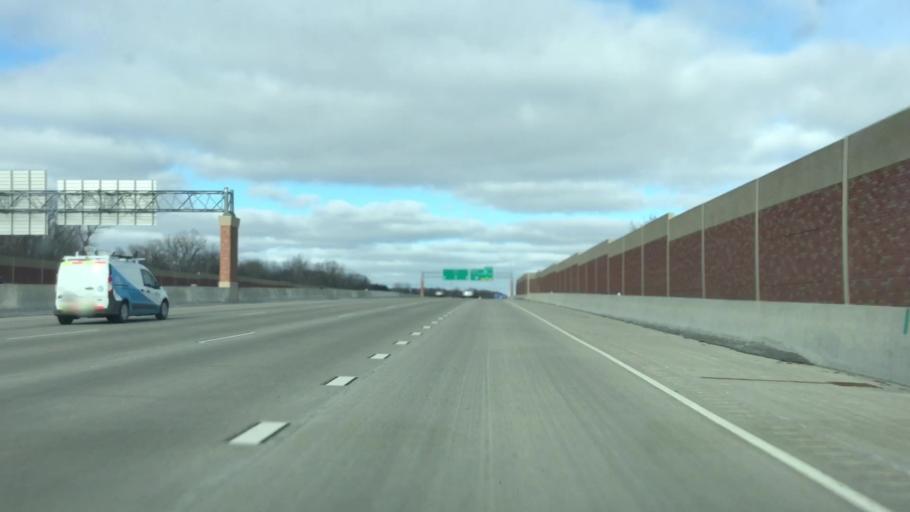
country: US
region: Wisconsin
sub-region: Brown County
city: Ashwaubenon
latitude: 44.5018
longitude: -88.0818
